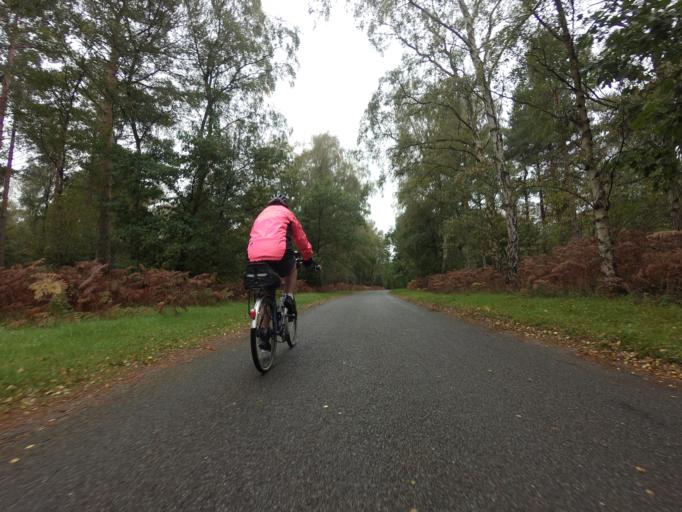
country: GB
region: England
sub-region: Norfolk
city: Dersingham
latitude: 52.8171
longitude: 0.4913
